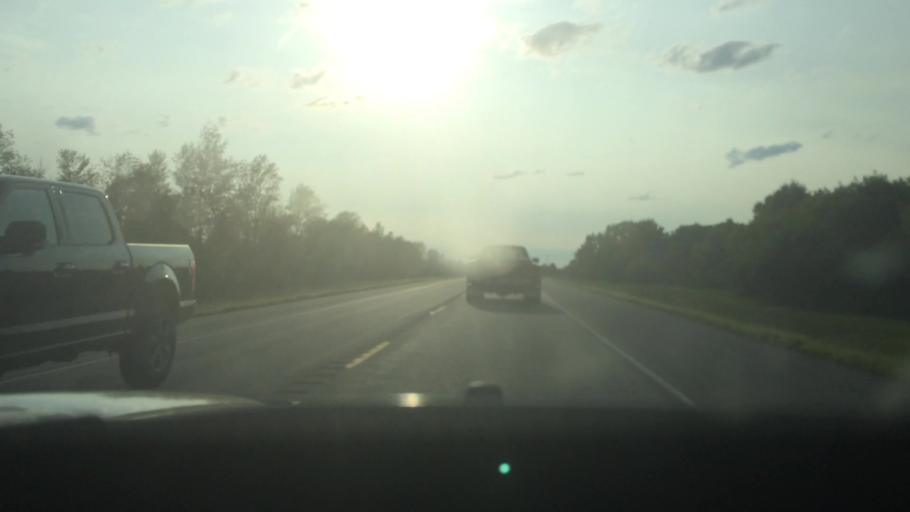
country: US
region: New York
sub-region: St. Lawrence County
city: Ogdensburg
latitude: 44.6790
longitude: -75.5081
